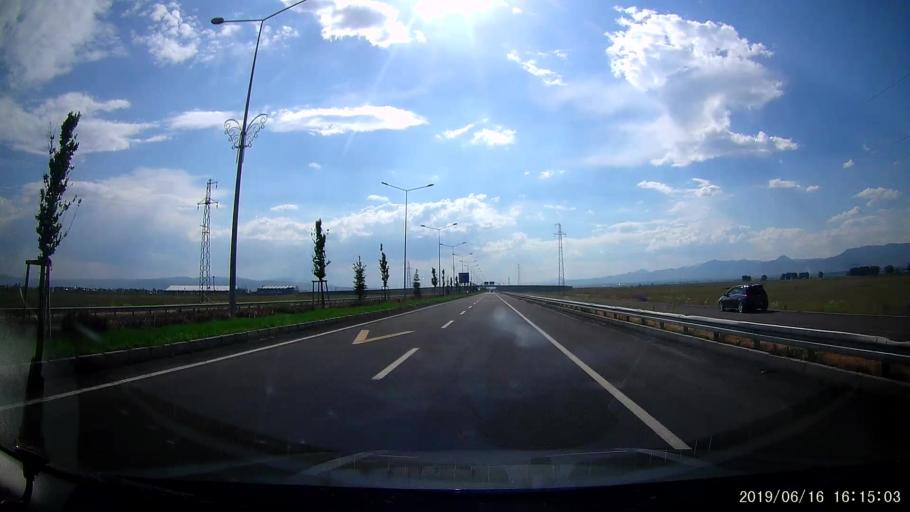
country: TR
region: Erzurum
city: Erzurum
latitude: 39.9615
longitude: 41.2343
